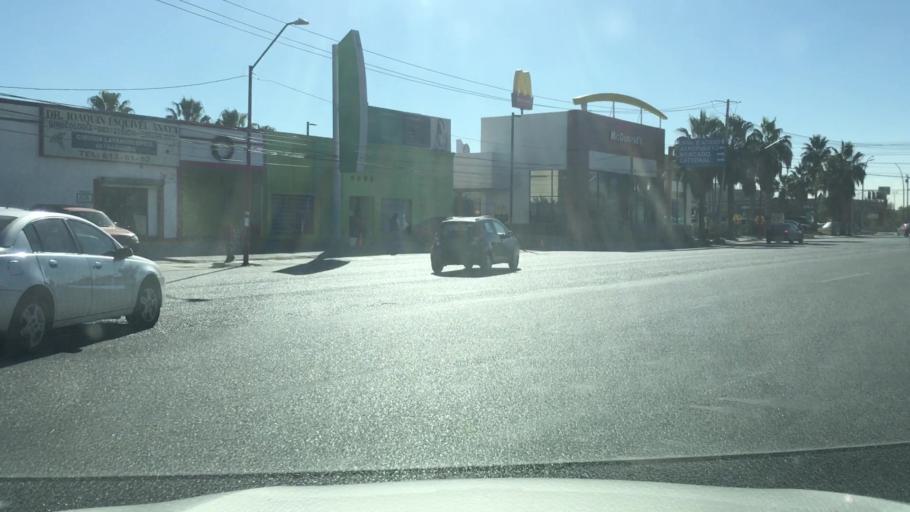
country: MX
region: Chihuahua
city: Ciudad Juarez
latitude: 31.7385
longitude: -106.4495
